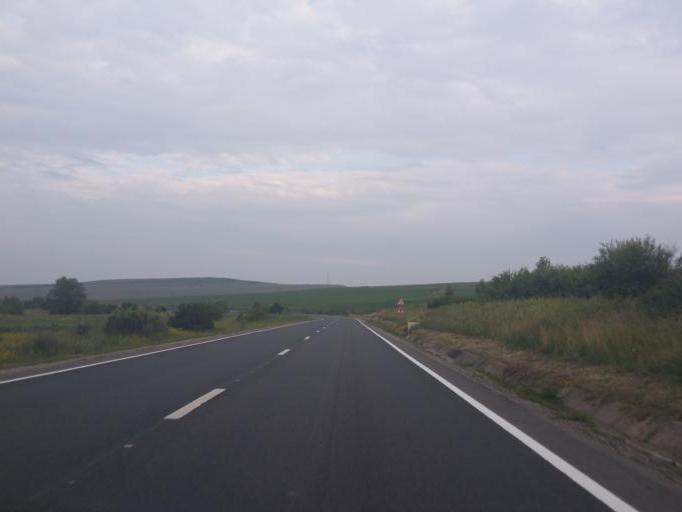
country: RO
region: Cluj
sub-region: Comuna Sanpaul
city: Sanpaul
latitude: 46.9241
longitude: 23.4082
